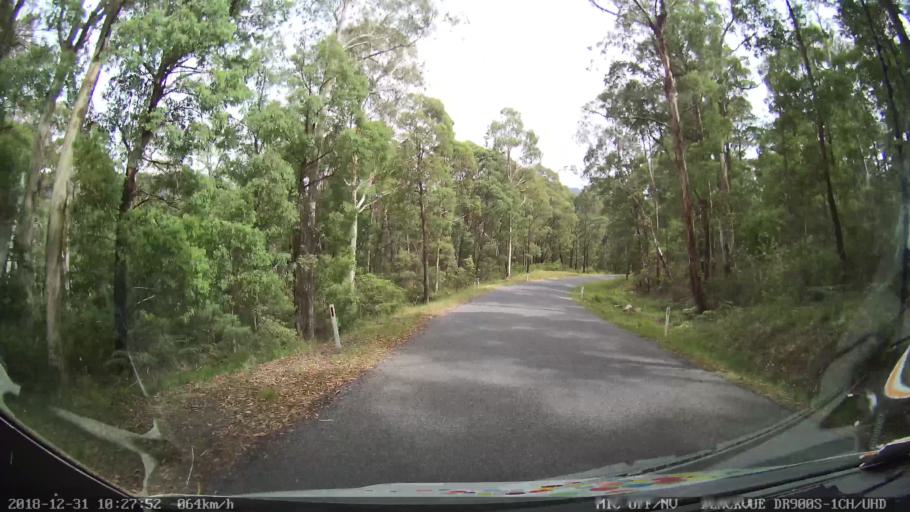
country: AU
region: New South Wales
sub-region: Snowy River
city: Jindabyne
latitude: -36.4831
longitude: 148.1439
